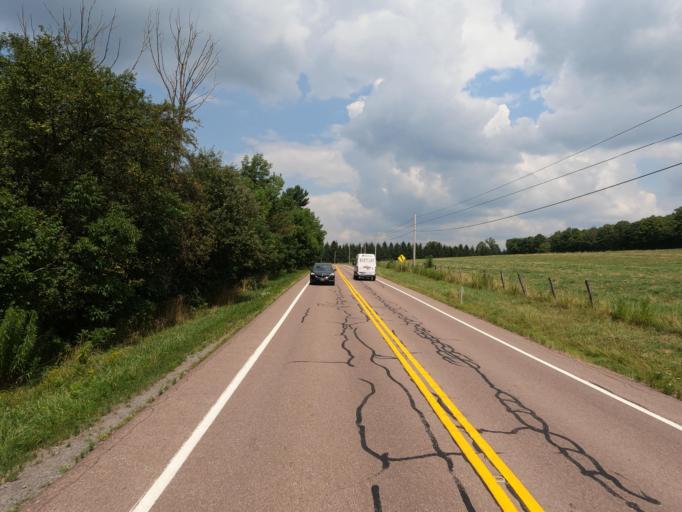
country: US
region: Maryland
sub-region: Allegany County
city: Westernport
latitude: 39.6381
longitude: -79.2048
